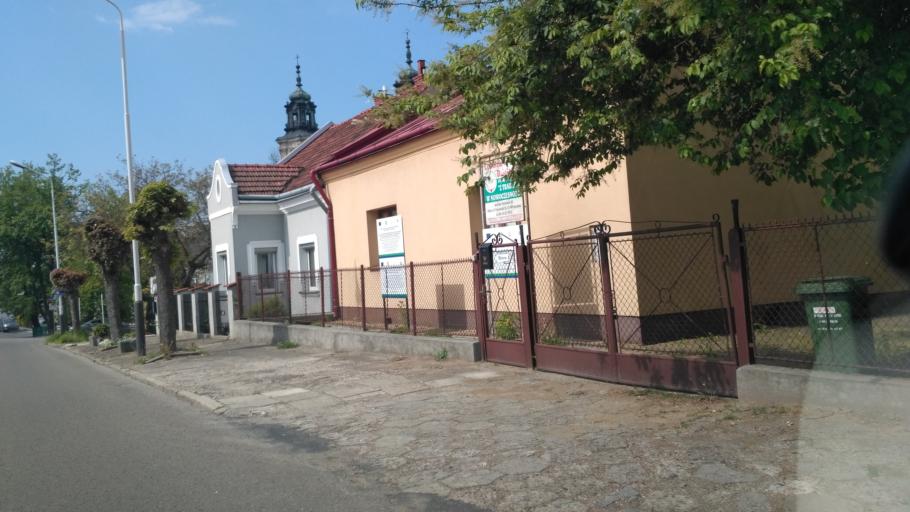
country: PL
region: Subcarpathian Voivodeship
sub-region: Powiat jaroslawski
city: Jaroslaw
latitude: 50.0172
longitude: 22.6670
